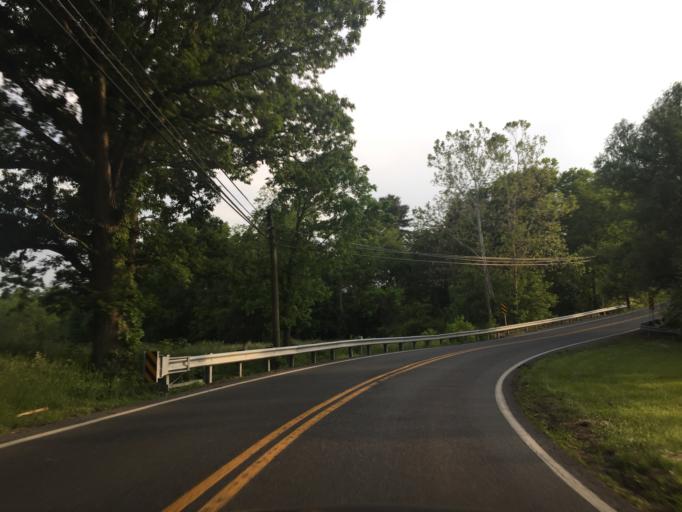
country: US
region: Maryland
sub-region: Frederick County
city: Adamstown
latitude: 39.3000
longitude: -77.5016
